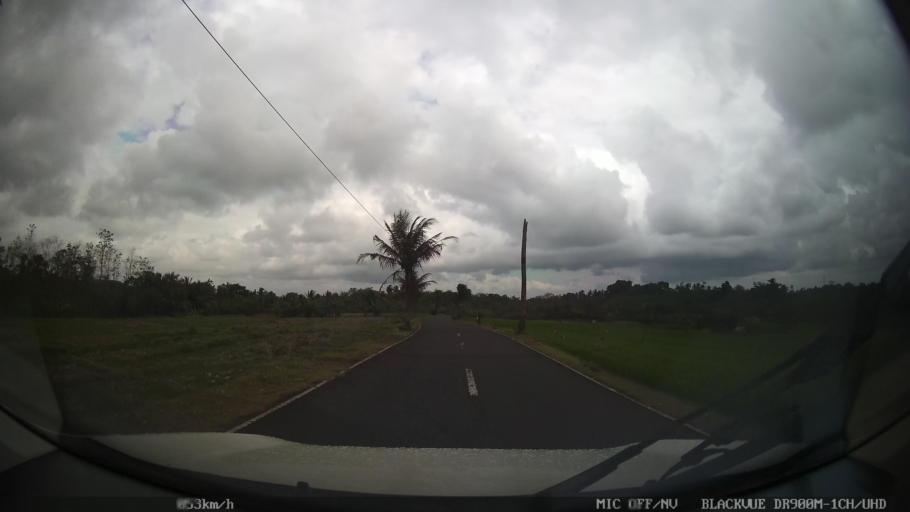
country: ID
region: Bali
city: Banjar Cemenggon
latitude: -8.5375
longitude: 115.1873
